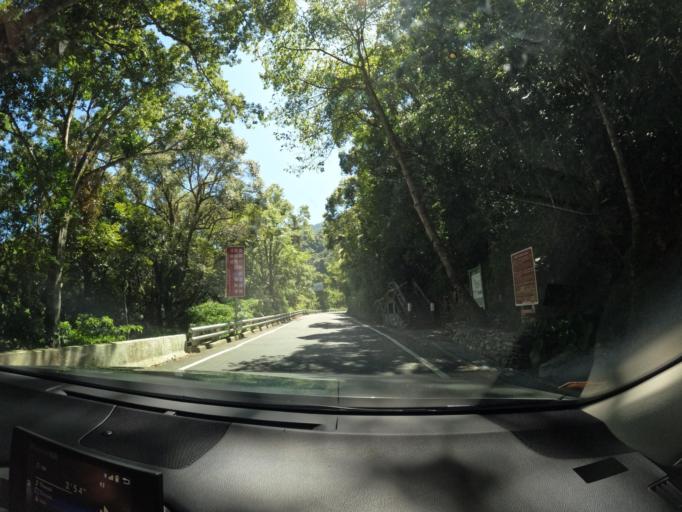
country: TW
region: Taiwan
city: Yujing
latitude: 23.2877
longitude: 120.8991
